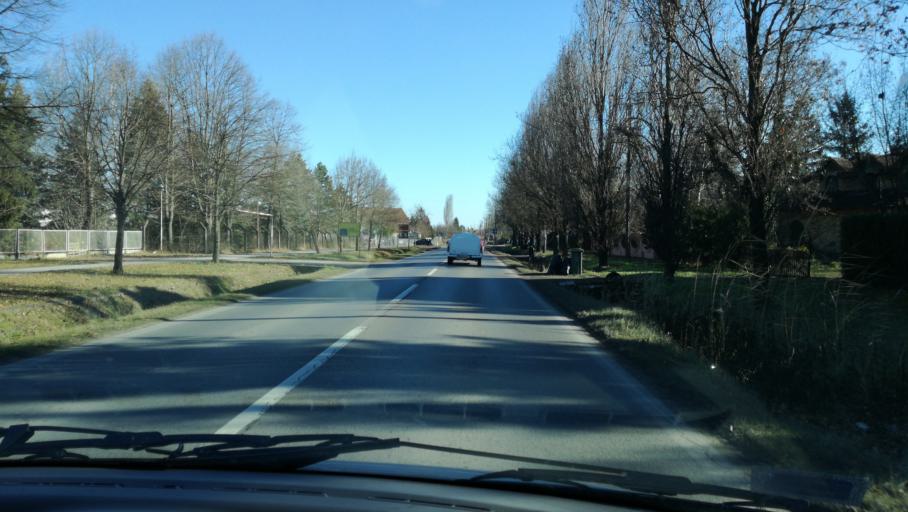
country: HU
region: Csongrad
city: Asotthalom
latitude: 46.1016
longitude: 19.7684
